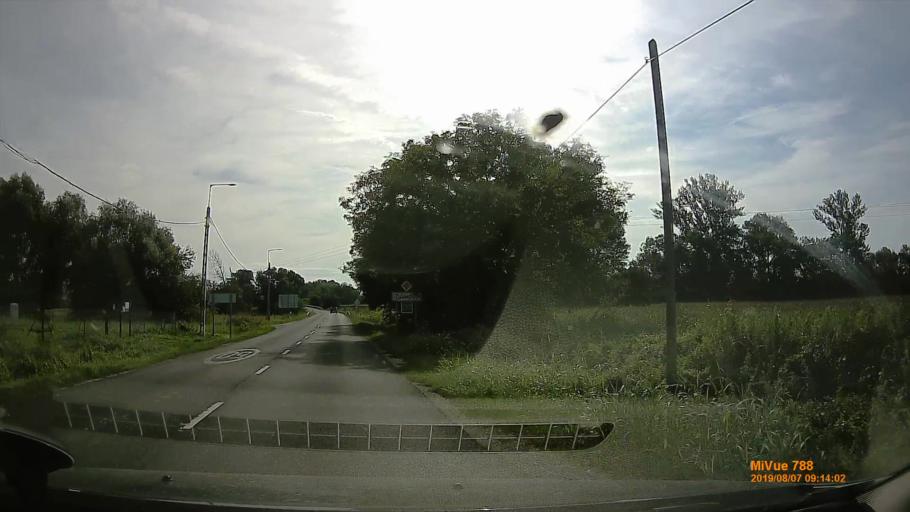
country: HU
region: Zala
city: Sarmellek
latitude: 46.7269
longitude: 17.1171
